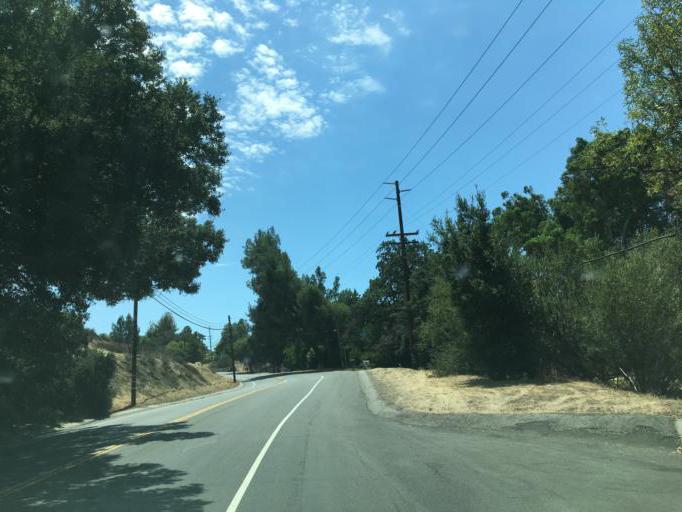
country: US
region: California
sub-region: Los Angeles County
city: Agoura Hills
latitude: 34.1378
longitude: -118.7567
